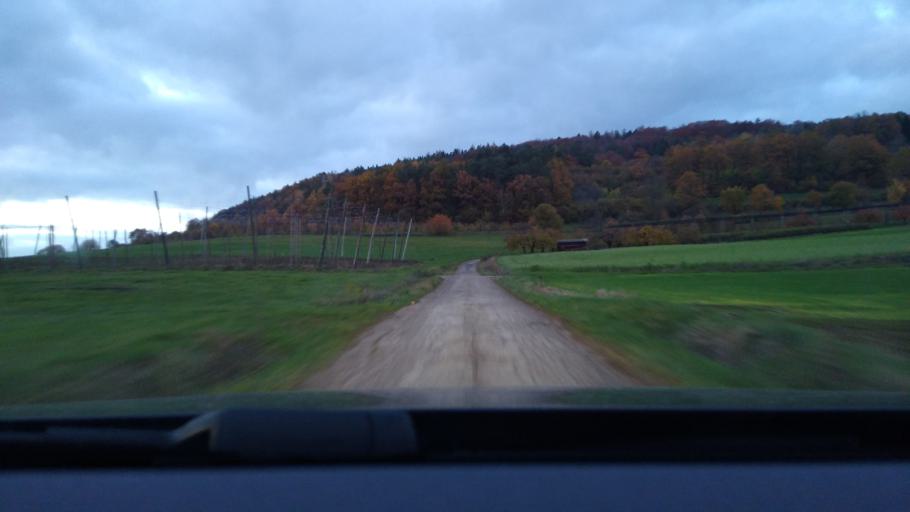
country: DE
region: Bavaria
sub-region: Upper Franconia
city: Igensdorf
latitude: 49.6274
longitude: 11.2387
